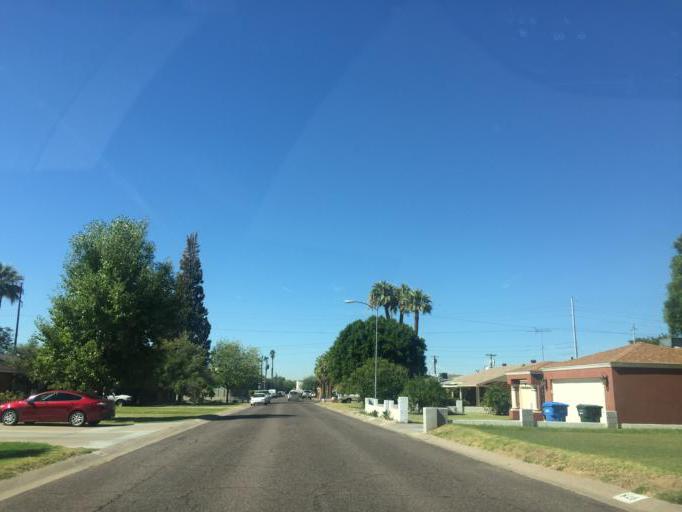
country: US
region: Arizona
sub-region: Maricopa County
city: Phoenix
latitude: 33.5373
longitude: -112.0616
